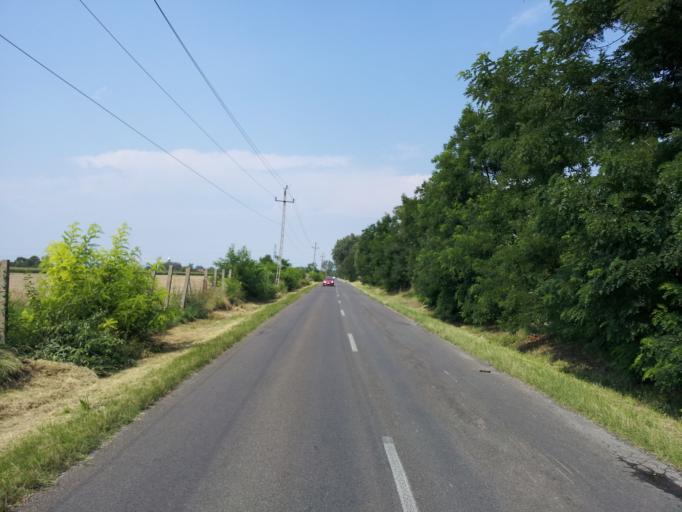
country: HU
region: Pest
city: Szigetcsep
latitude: 47.2509
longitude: 18.9641
